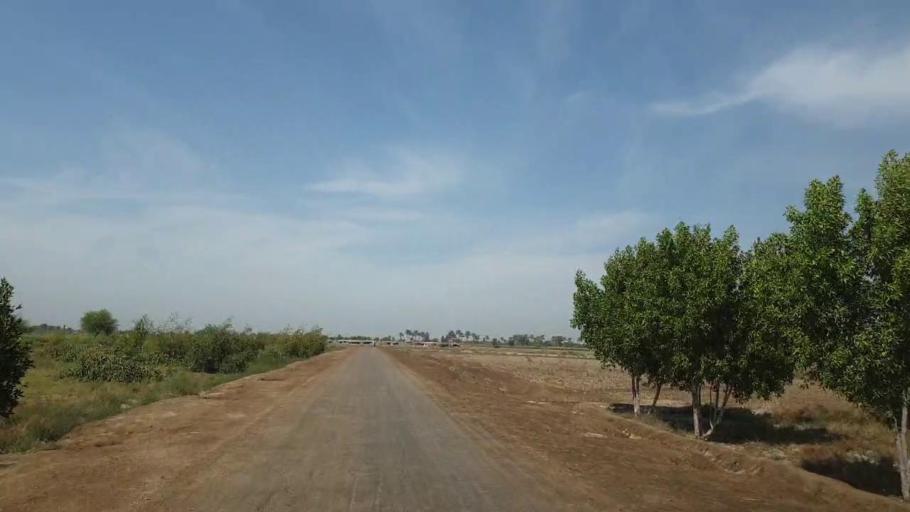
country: PK
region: Sindh
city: Kunri
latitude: 25.2136
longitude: 69.5367
